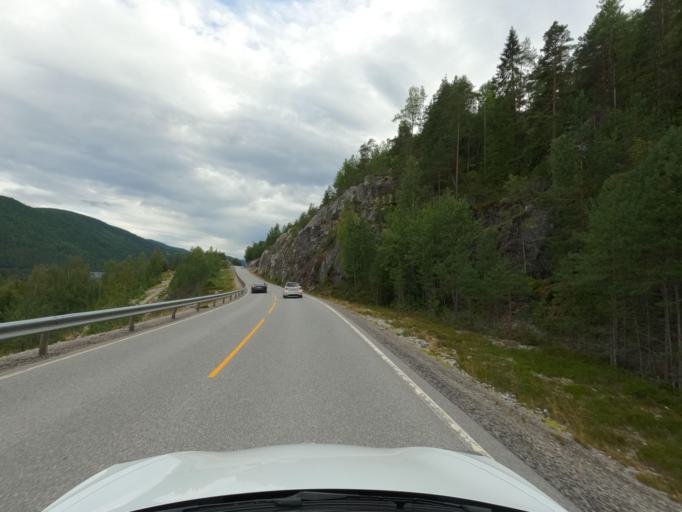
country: NO
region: Telemark
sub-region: Hjartdal
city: Sauland
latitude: 59.7675
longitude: 9.0178
